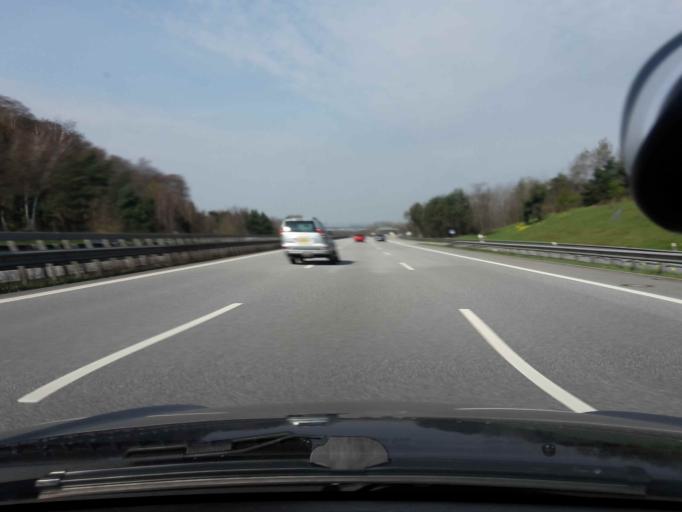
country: DE
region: Hamburg
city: Harburg
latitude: 53.4681
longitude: 9.9236
